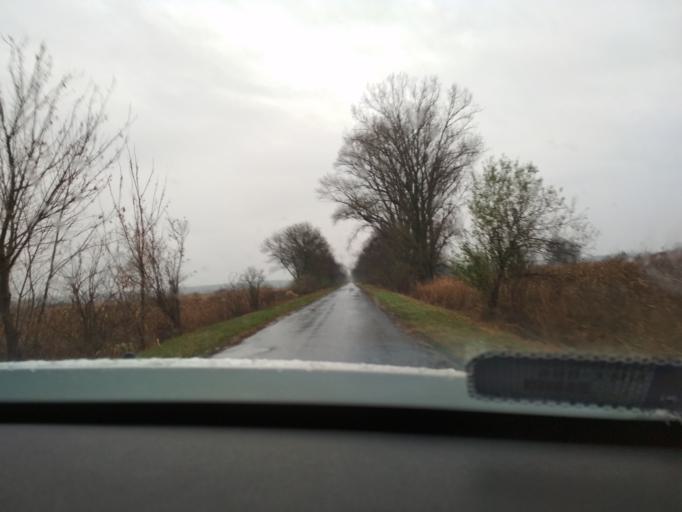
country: HU
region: Csongrad
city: Baks
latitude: 46.5398
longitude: 20.1278
